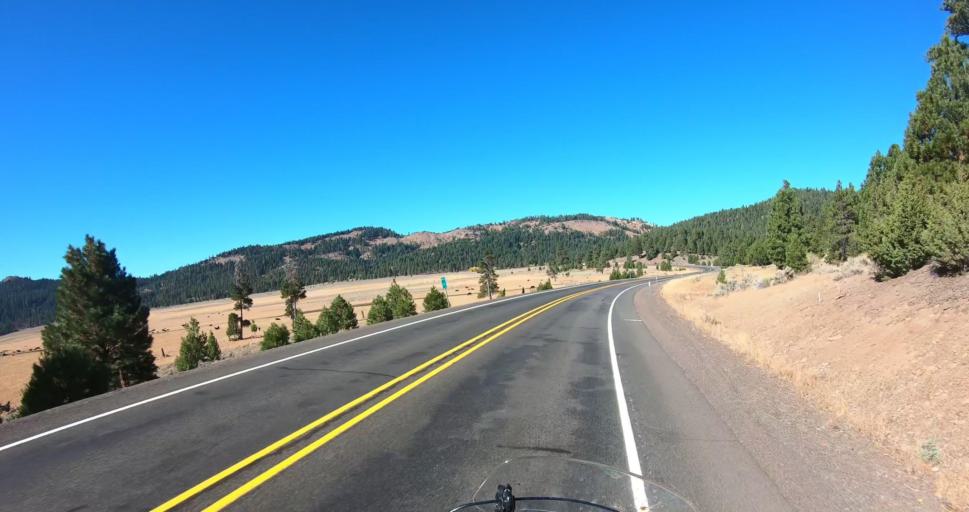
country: US
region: Oregon
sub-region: Lake County
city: Lakeview
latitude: 42.2284
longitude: -120.2694
